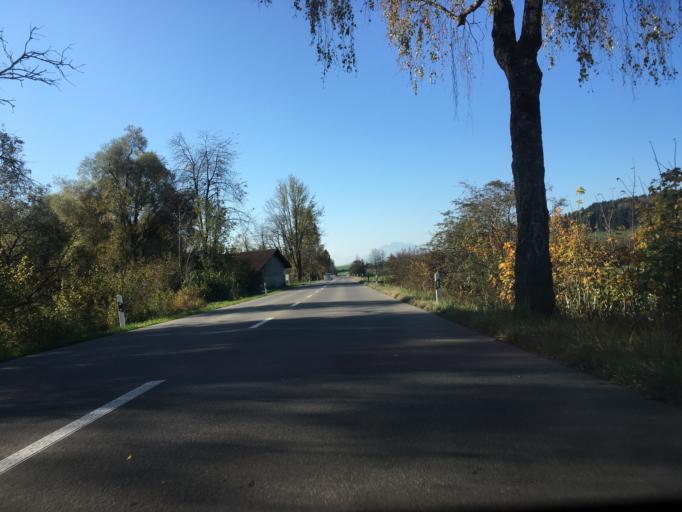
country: CH
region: Zurich
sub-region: Bezirk Affoltern
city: Hausen am Albis / Hausen (Dorf)
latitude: 47.2249
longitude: 8.5255
